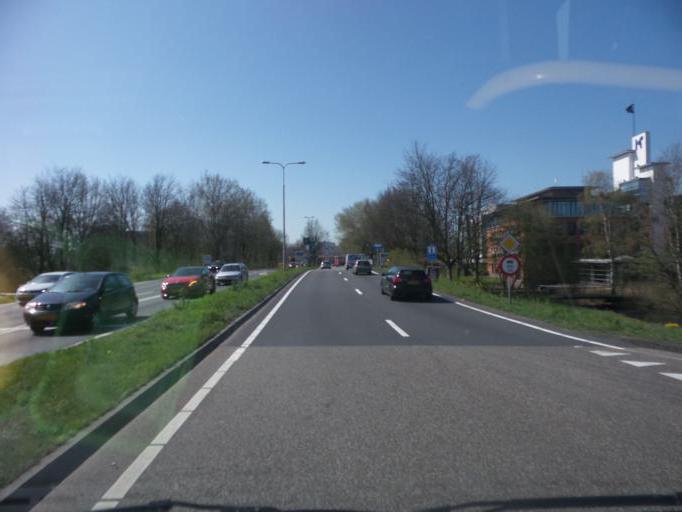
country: NL
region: South Holland
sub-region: Gemeente Gouda
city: Bloemendaal
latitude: 52.0269
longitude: 4.6836
